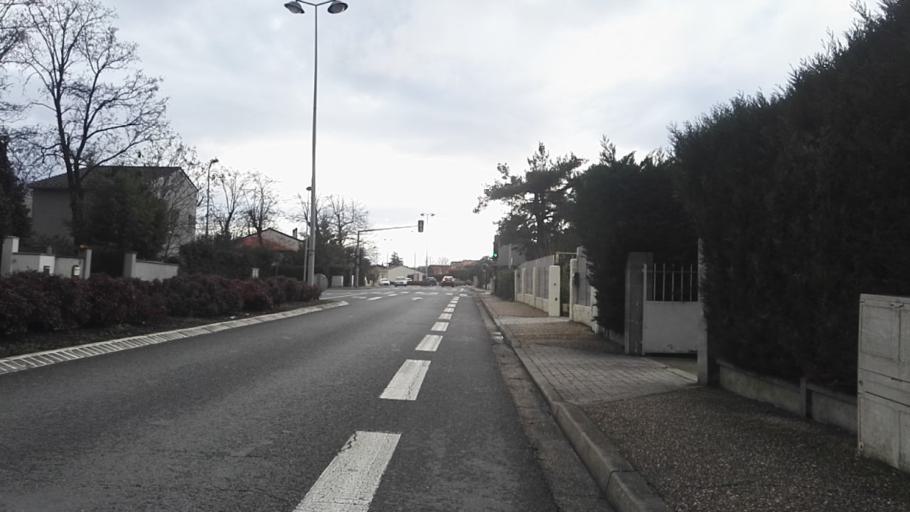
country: FR
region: Aquitaine
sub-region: Departement de la Gironde
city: Eysines
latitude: 44.8670
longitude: -0.6375
